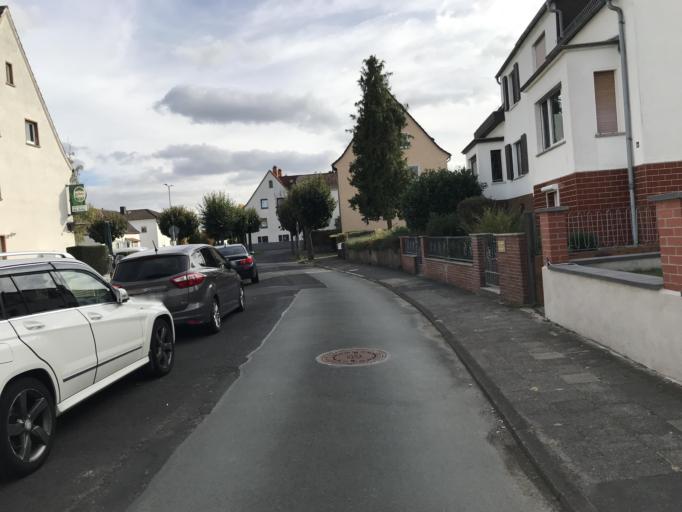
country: DE
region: Hesse
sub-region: Regierungsbezirk Darmstadt
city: Butzbach
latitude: 50.4361
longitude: 8.6560
